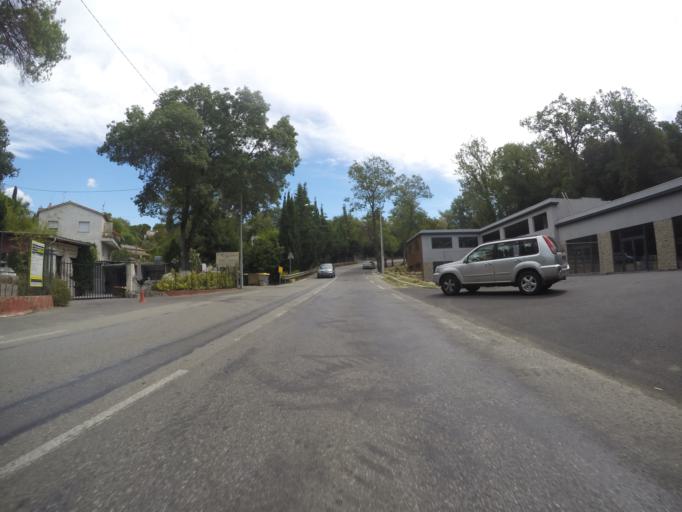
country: FR
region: Provence-Alpes-Cote d'Azur
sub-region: Departement des Alpes-Maritimes
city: Mougins
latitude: 43.6062
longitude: 6.9976
